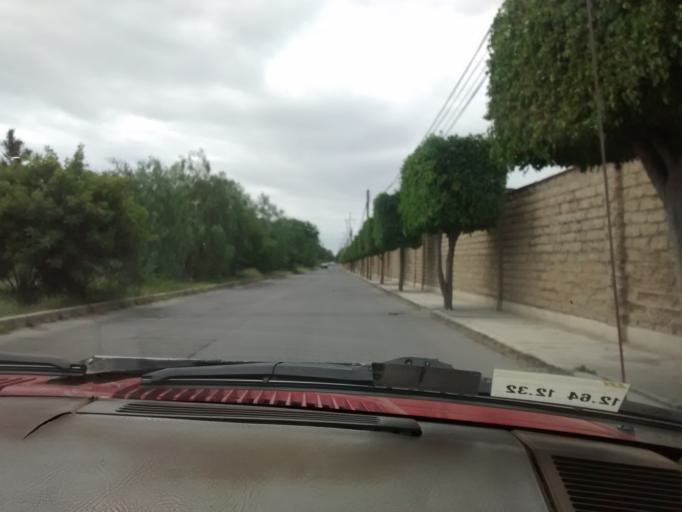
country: MX
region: Puebla
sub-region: Santiago Miahuatlan
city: San Isidro Vista Hermosa
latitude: 18.4820
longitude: -97.4130
